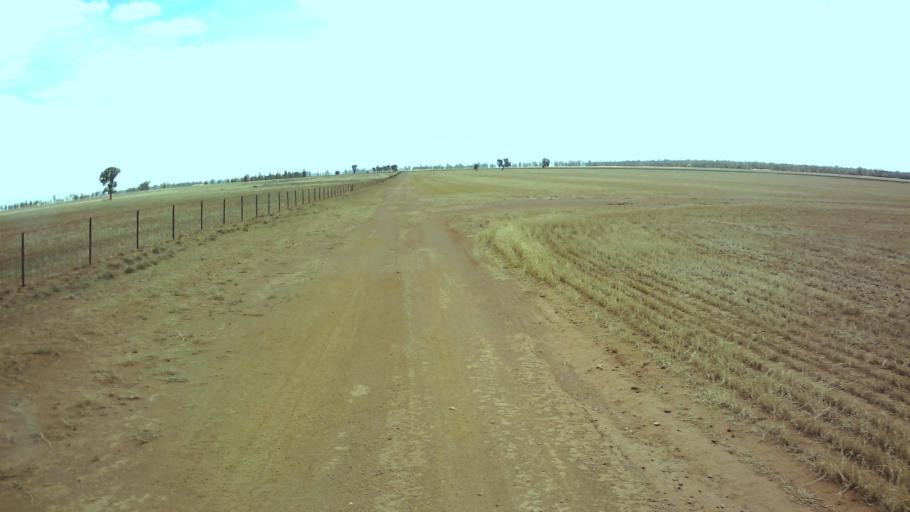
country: AU
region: New South Wales
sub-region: Weddin
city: Grenfell
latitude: -33.9061
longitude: 147.7381
